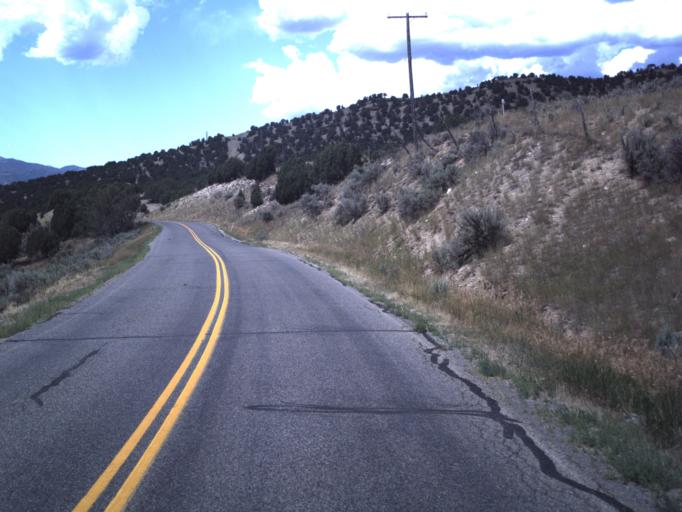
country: US
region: Utah
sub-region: Summit County
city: Oakley
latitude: 40.7583
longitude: -111.3743
